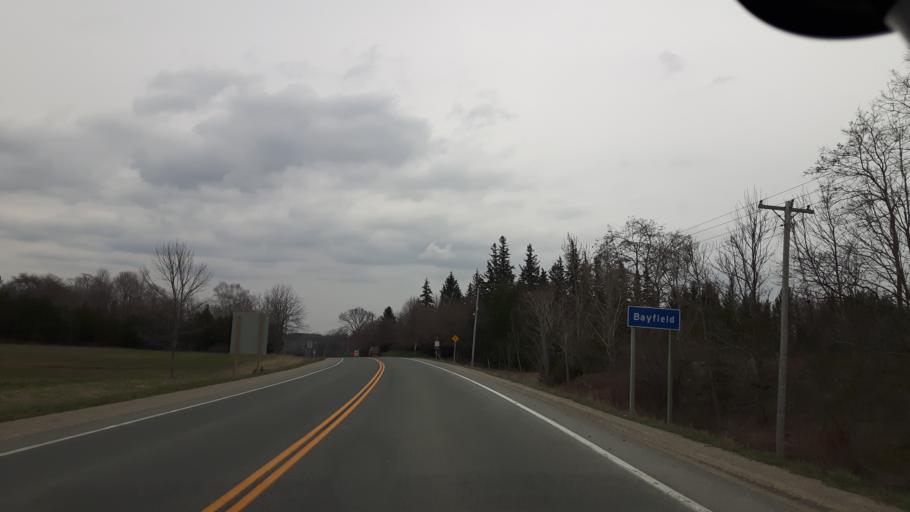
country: CA
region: Ontario
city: Bluewater
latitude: 43.5729
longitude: -81.7039
